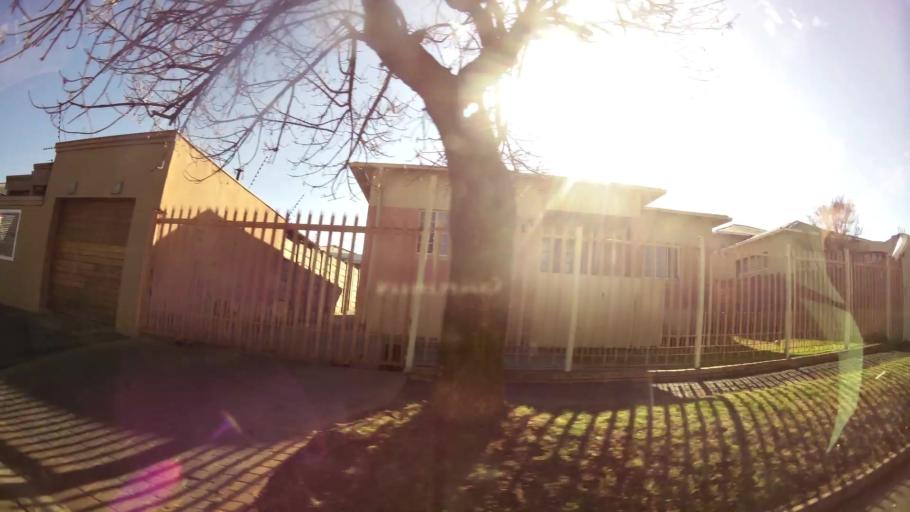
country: ZA
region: Gauteng
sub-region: City of Johannesburg Metropolitan Municipality
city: Johannesburg
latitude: -26.1993
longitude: 27.9948
